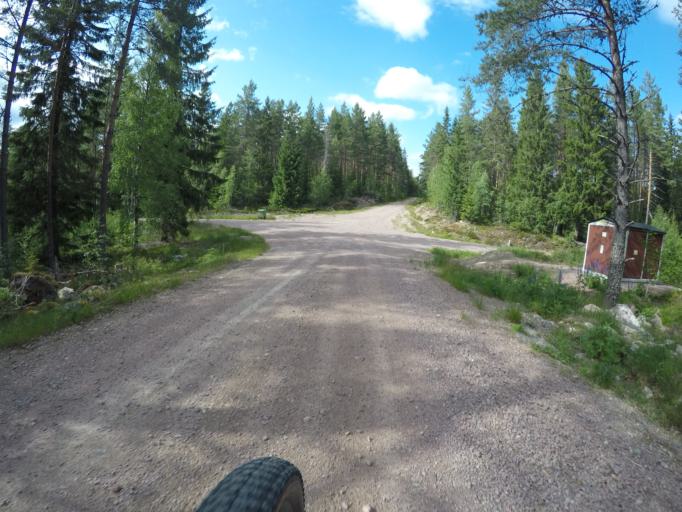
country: SE
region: Dalarna
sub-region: Ludvika Kommun
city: Abborrberget
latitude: 60.0957
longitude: 14.5464
